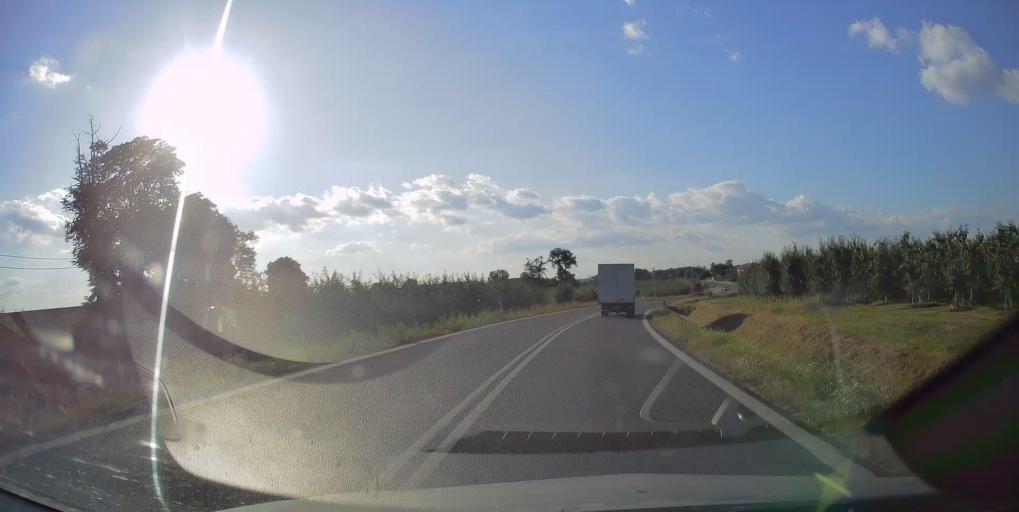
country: PL
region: Lodz Voivodeship
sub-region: Powiat rawski
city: Biala Rawska
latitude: 51.8035
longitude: 20.5041
